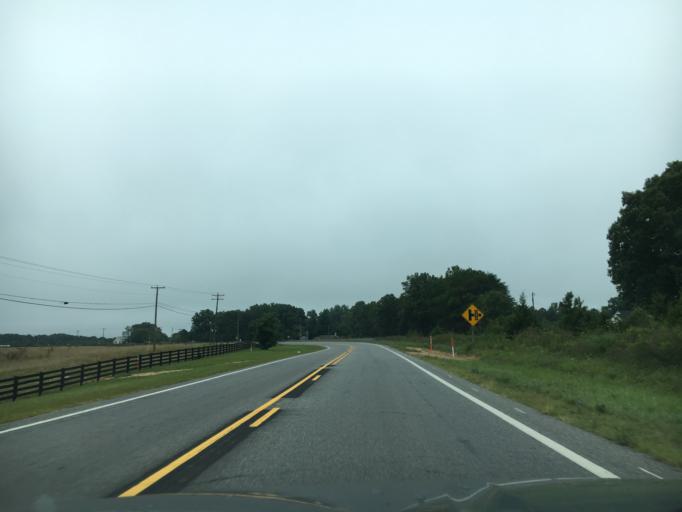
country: US
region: Virginia
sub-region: Campbell County
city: Brookneal
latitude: 37.0783
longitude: -78.9853
